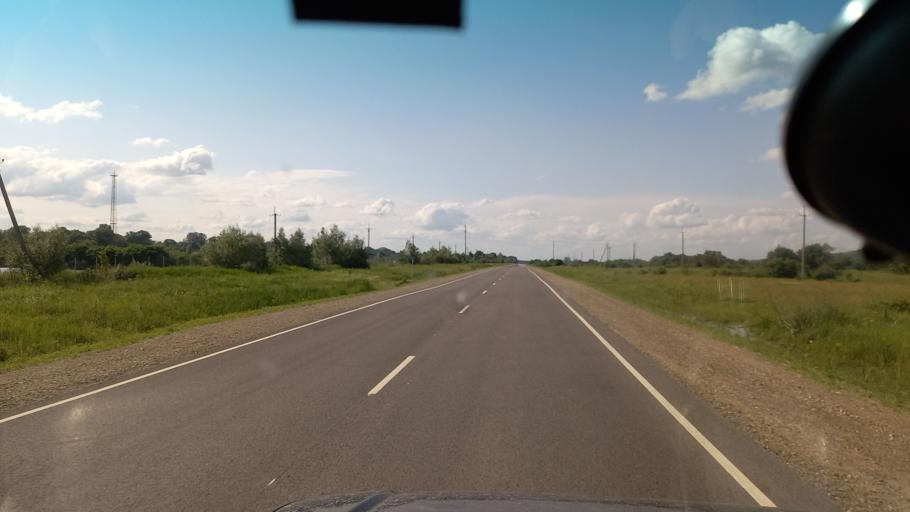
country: RU
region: Krasnodarskiy
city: Mostovskoy
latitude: 44.3892
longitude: 40.8477
